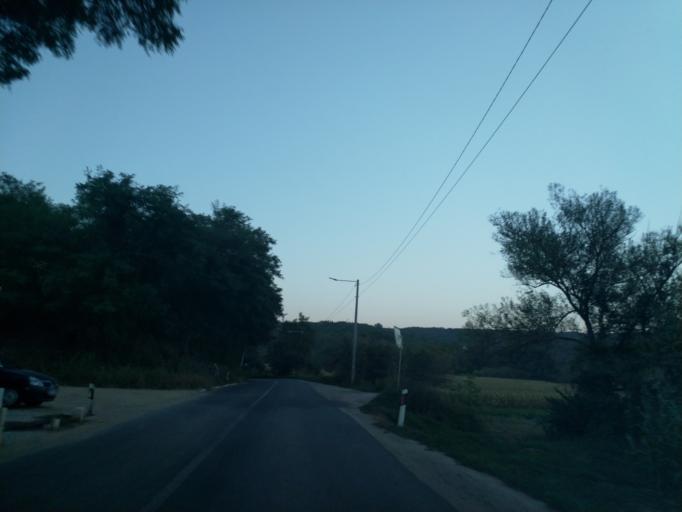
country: RS
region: Central Serbia
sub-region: Rasinski Okrug
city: Krusevac
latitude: 43.6249
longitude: 21.3303
